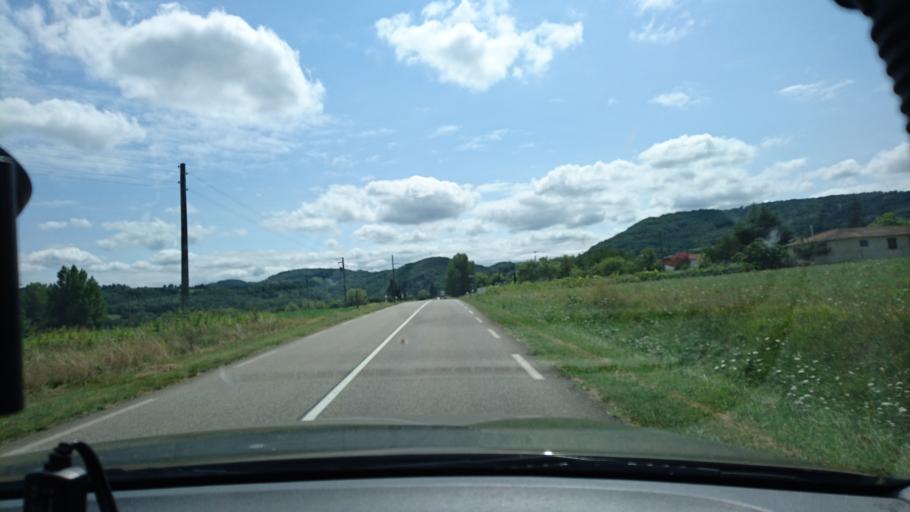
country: FR
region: Midi-Pyrenees
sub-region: Departement de la Haute-Garonne
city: Gaillac-Toulza
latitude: 43.1148
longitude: 1.4408
